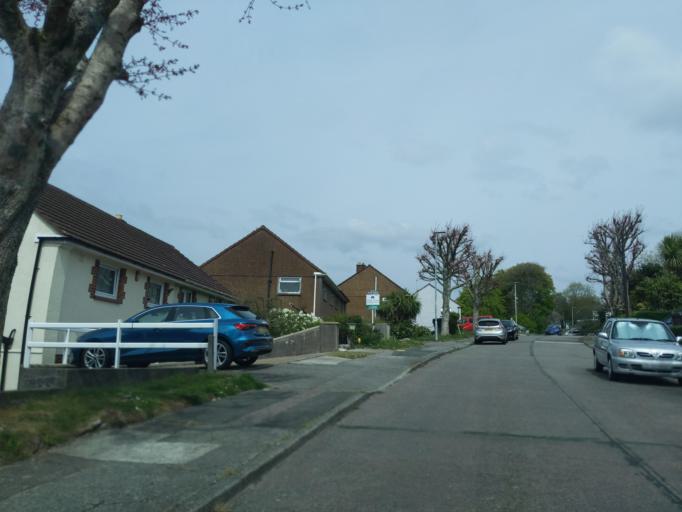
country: GB
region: England
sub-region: Plymouth
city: Plymouth
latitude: 50.4130
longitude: -4.1368
